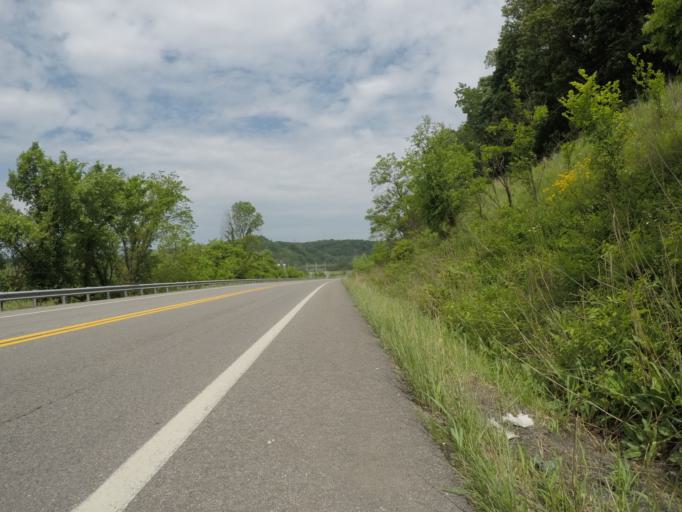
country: US
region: West Virginia
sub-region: Wayne County
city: Kenova
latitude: 38.3421
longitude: -82.5892
